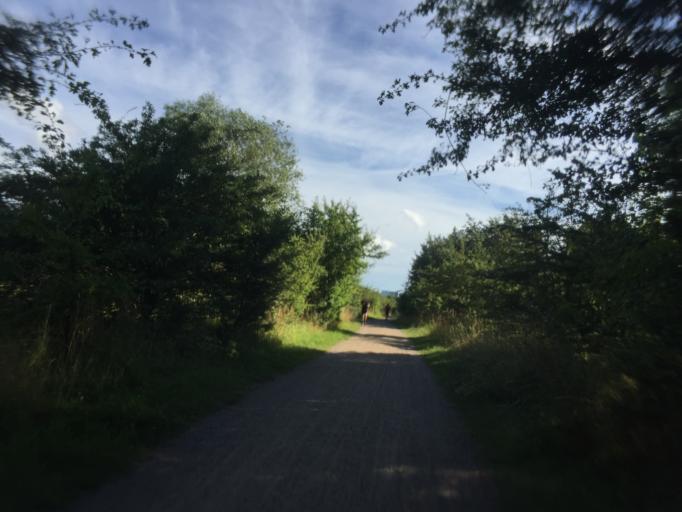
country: DK
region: Capital Region
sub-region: Kobenhavn
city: Christianshavn
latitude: 55.6515
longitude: 12.5830
